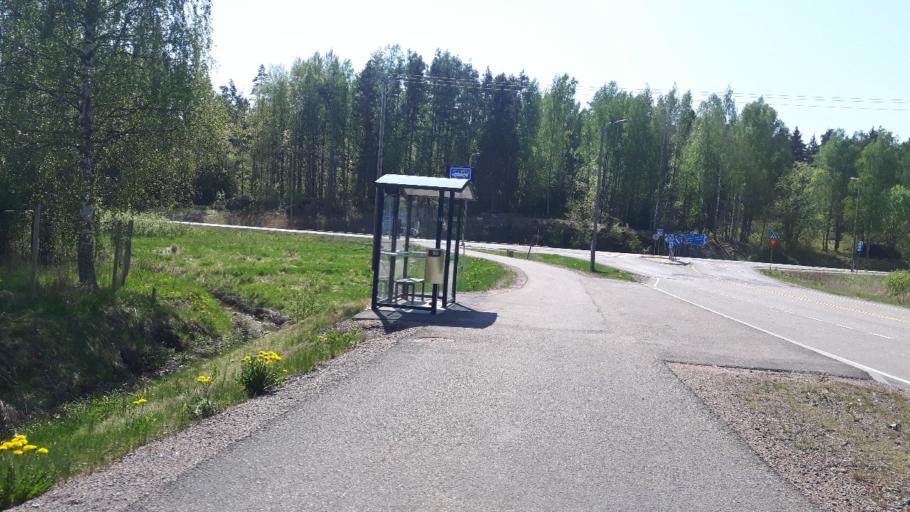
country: FI
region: Uusimaa
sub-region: Loviisa
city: Ruotsinpyhtaeae
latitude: 60.4961
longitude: 26.4417
